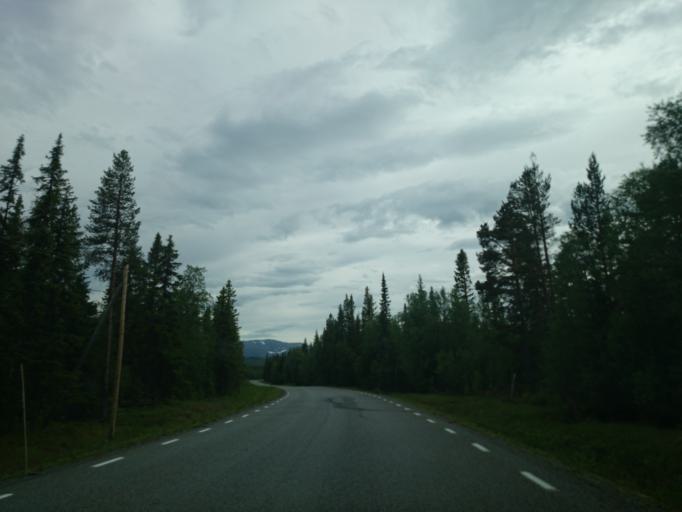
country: SE
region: Jaemtland
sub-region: Are Kommun
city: Are
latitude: 63.2112
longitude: 13.1598
